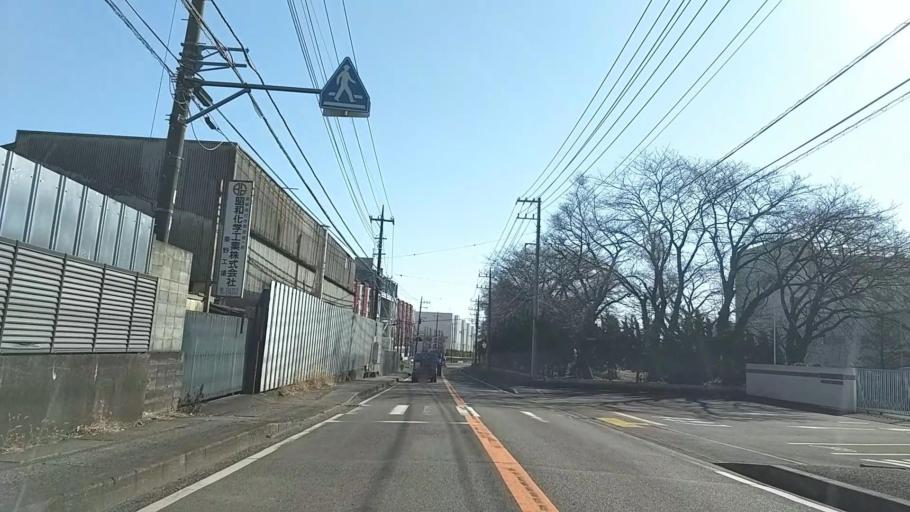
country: JP
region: Kanagawa
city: Hadano
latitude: 35.3895
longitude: 139.2049
